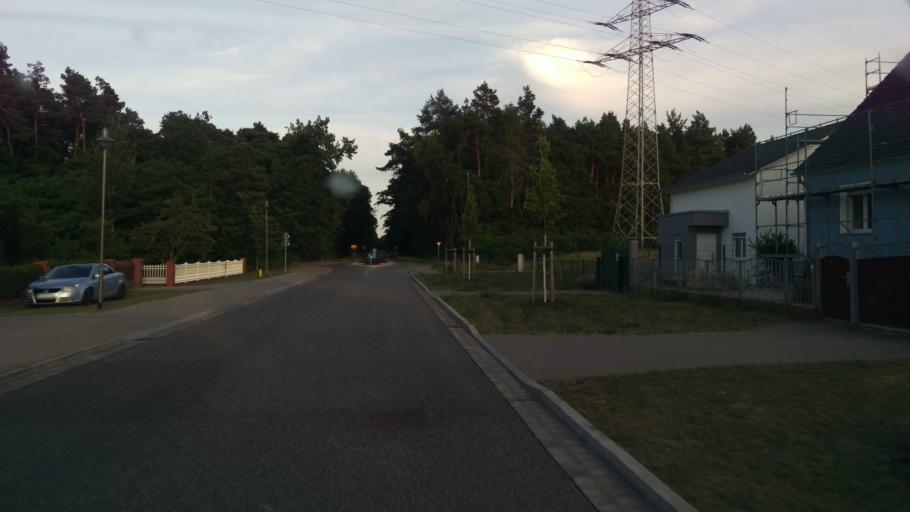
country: DE
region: Brandenburg
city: Ziltendorf
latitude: 52.2009
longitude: 14.6322
